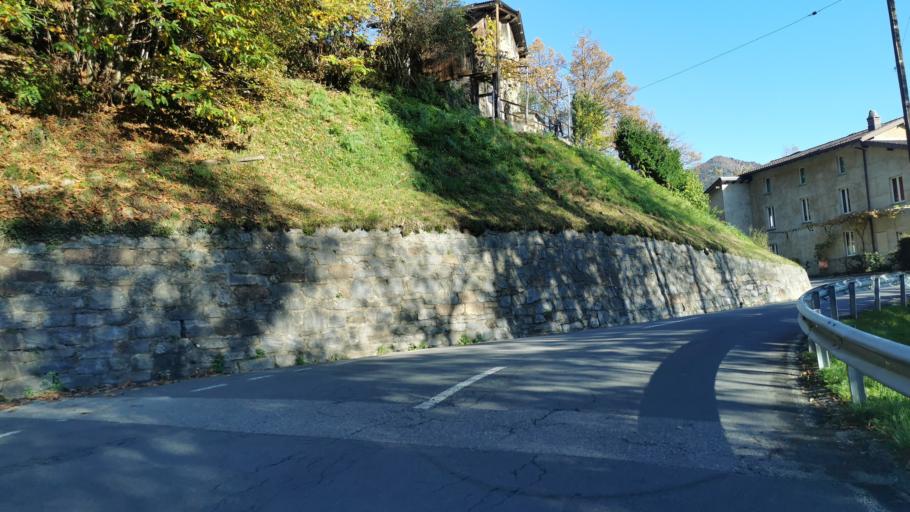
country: CH
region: Ticino
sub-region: Lugano District
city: Pura
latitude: 46.0155
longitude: 8.8560
